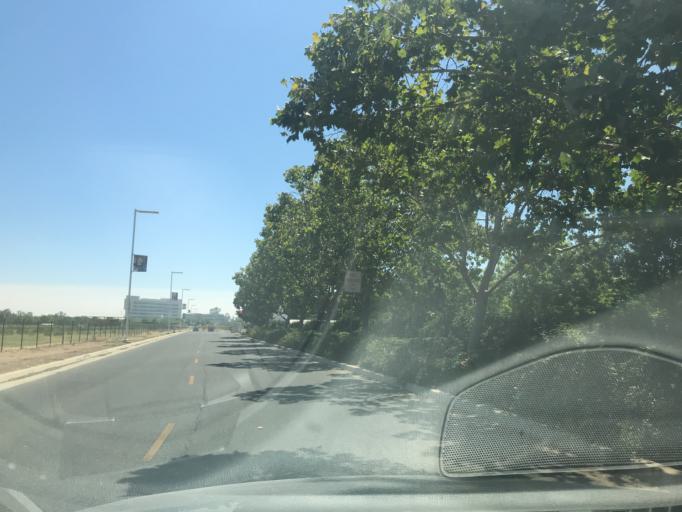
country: US
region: California
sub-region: Merced County
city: Merced
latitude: 37.3393
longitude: -120.4760
